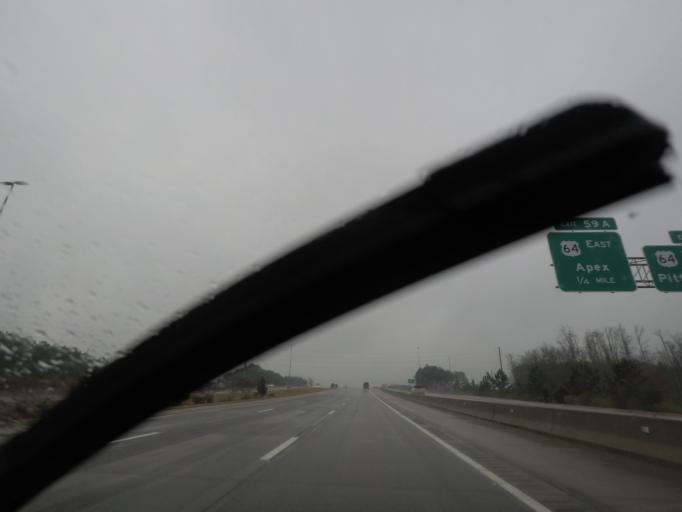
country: US
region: North Carolina
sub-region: Wake County
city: Green Level
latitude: 35.7519
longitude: -78.8921
